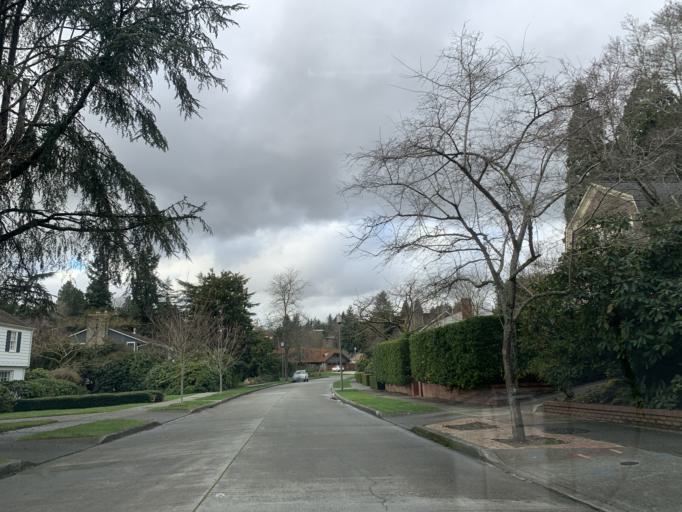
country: US
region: Washington
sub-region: King County
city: Yarrow Point
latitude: 47.6666
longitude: -122.2672
